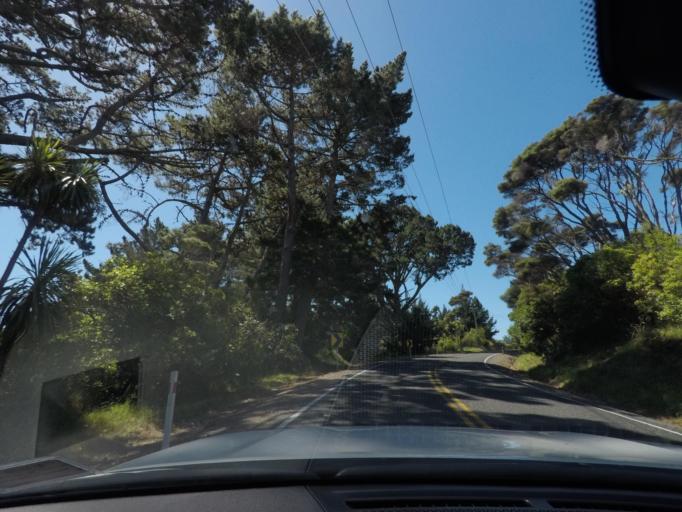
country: NZ
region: Auckland
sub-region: Auckland
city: Parakai
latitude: -36.6042
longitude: 174.3341
